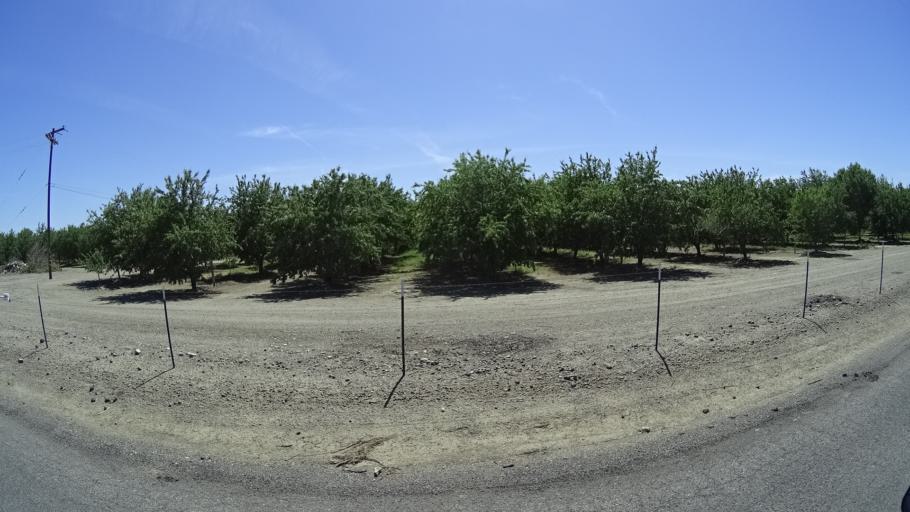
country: US
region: California
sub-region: Glenn County
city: Orland
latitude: 39.7324
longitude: -122.1442
